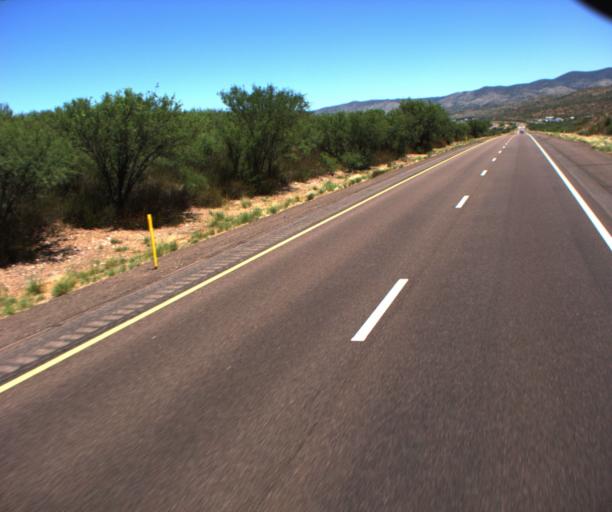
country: US
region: Arizona
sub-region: Gila County
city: Payson
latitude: 34.0761
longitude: -111.3570
